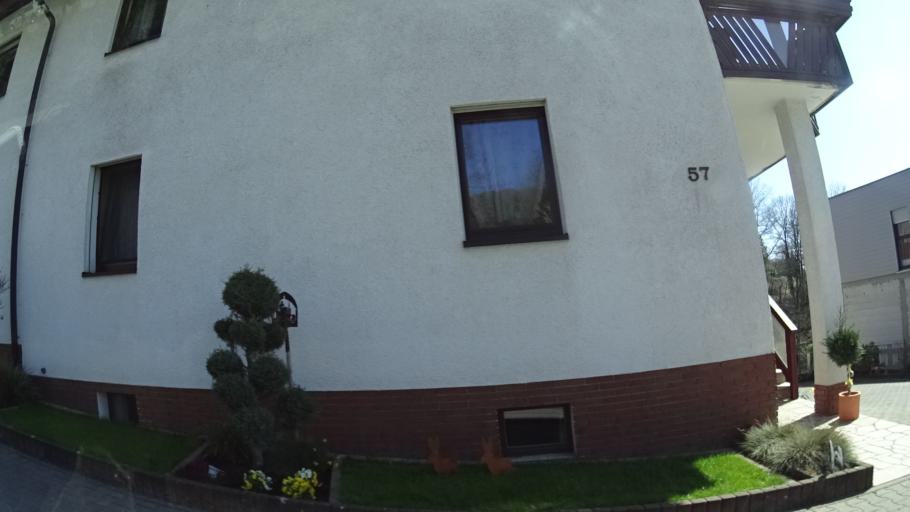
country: DE
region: Hesse
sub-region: Regierungsbezirk Darmstadt
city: Wald-Michelbach
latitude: 49.5883
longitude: 8.8147
